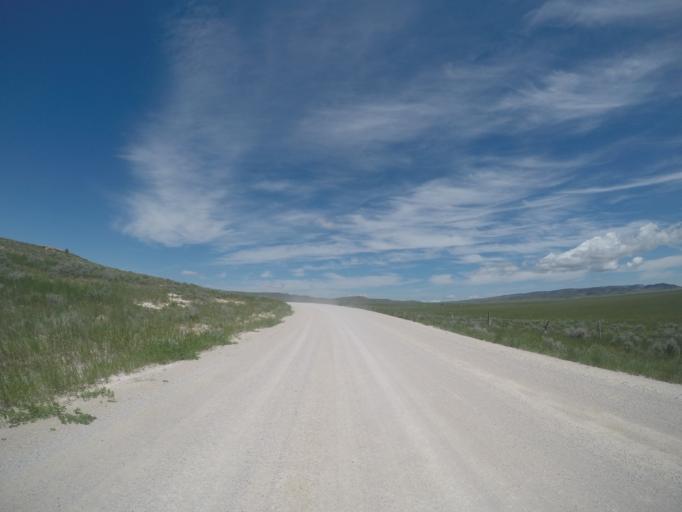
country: US
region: Wyoming
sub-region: Park County
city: Powell
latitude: 45.2062
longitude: -108.7273
